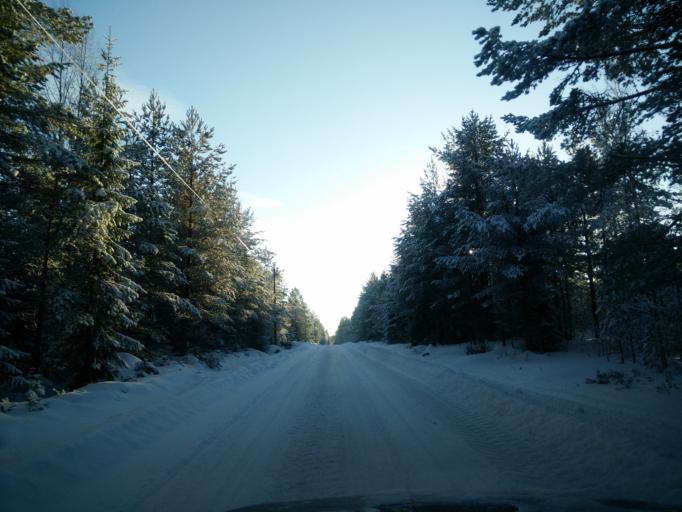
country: SE
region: Vaesternorrland
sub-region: Sundsvalls Kommun
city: Njurundabommen
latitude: 62.2172
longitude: 17.4934
